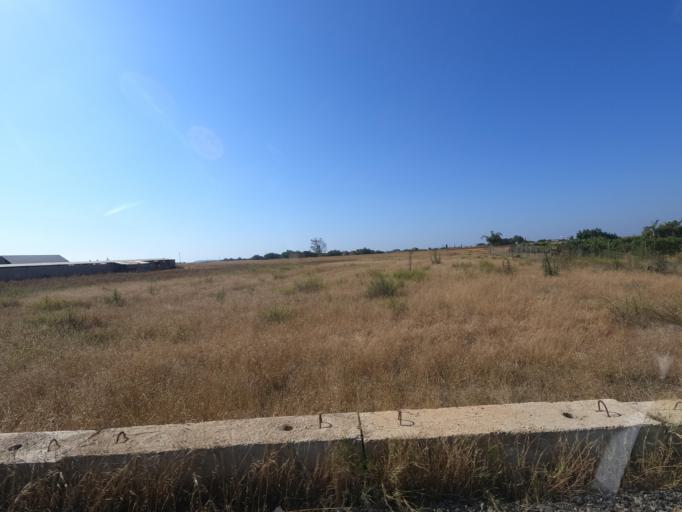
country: CY
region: Ammochostos
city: Frenaros
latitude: 35.0446
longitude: 33.9363
